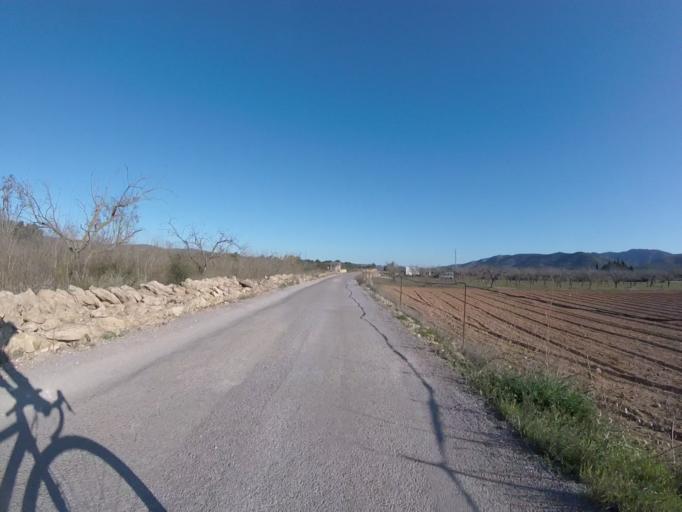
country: ES
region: Valencia
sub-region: Provincia de Castello
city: Alcala de Xivert
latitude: 40.2879
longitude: 0.2144
